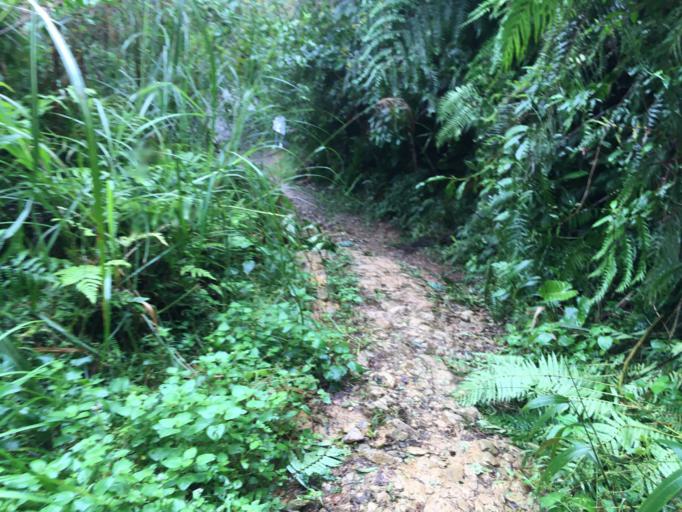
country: TW
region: Taiwan
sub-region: Yilan
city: Yilan
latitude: 24.6759
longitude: 121.5730
